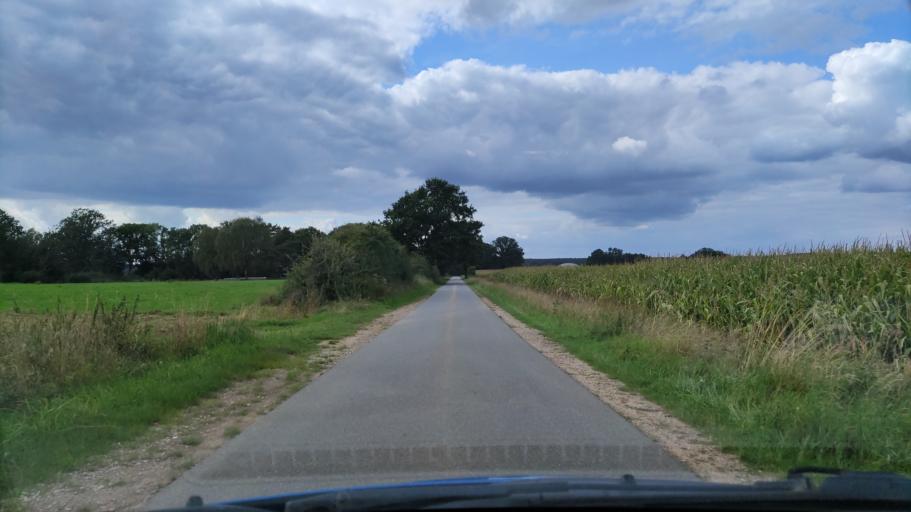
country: DE
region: Lower Saxony
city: Romstedt
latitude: 53.0790
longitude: 10.6545
